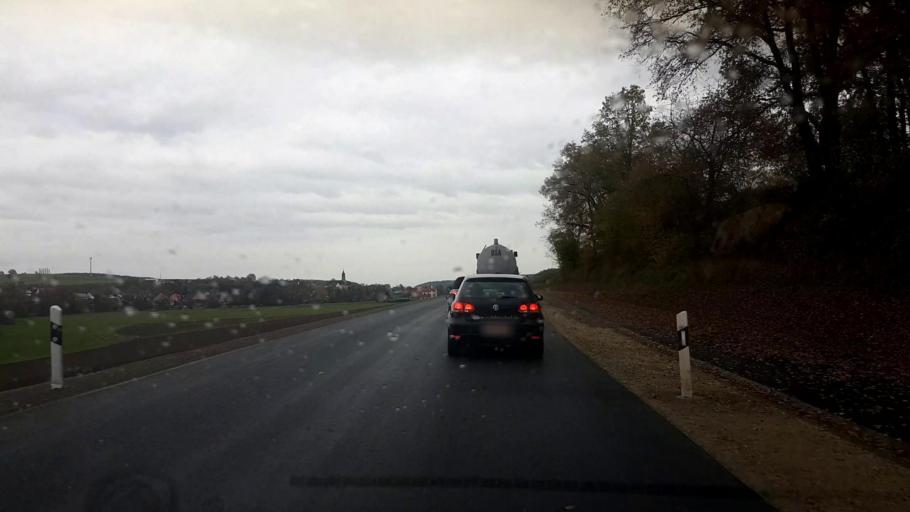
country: DE
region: Bavaria
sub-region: Upper Franconia
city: Burgwindheim
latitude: 49.8762
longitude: 10.6126
